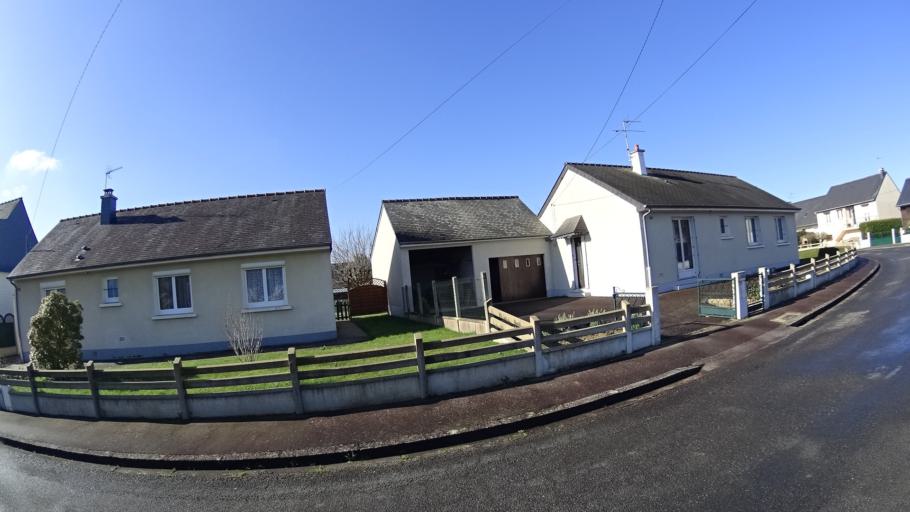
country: FR
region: Brittany
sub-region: Departement d'Ille-et-Vilaine
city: Breteil
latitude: 48.1455
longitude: -1.8966
